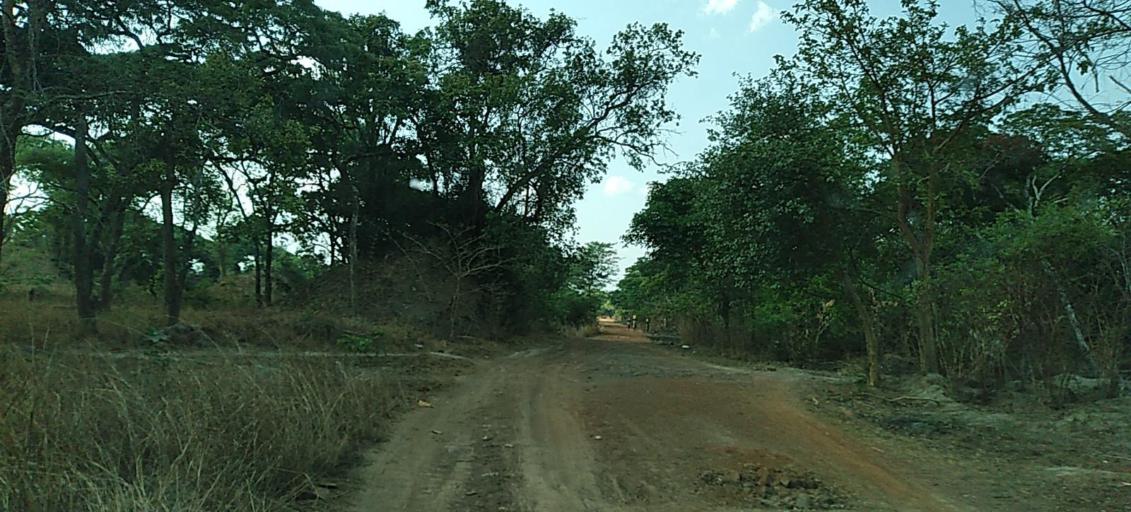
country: ZM
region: Copperbelt
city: Mpongwe
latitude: -13.4629
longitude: 28.0687
